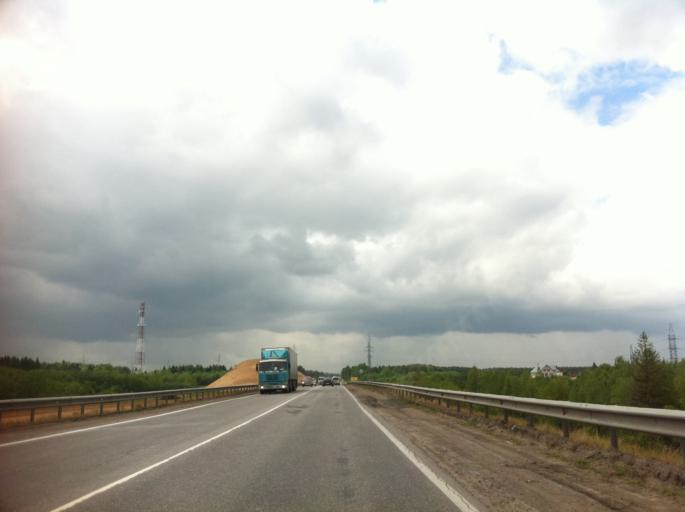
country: RU
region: Leningrad
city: Gatchina
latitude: 59.5269
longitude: 30.1214
